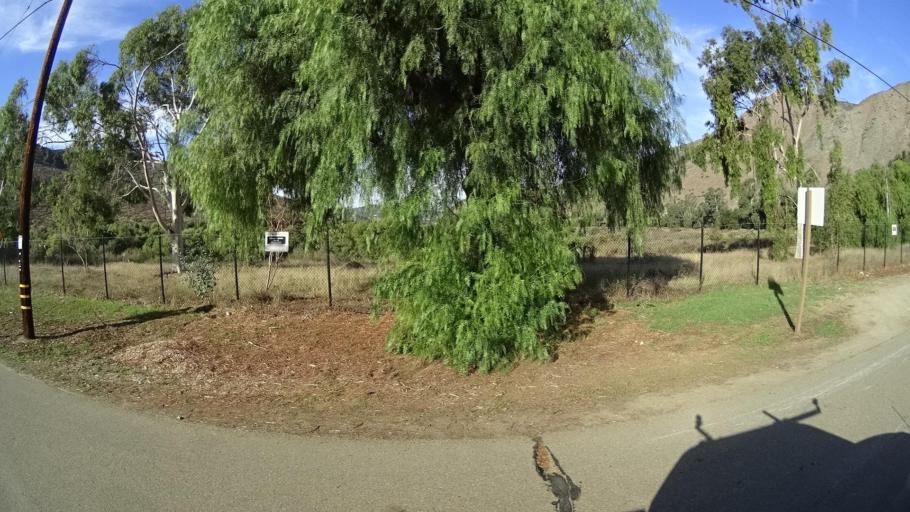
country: US
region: California
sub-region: San Diego County
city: Crest
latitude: 32.7801
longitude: -116.8522
